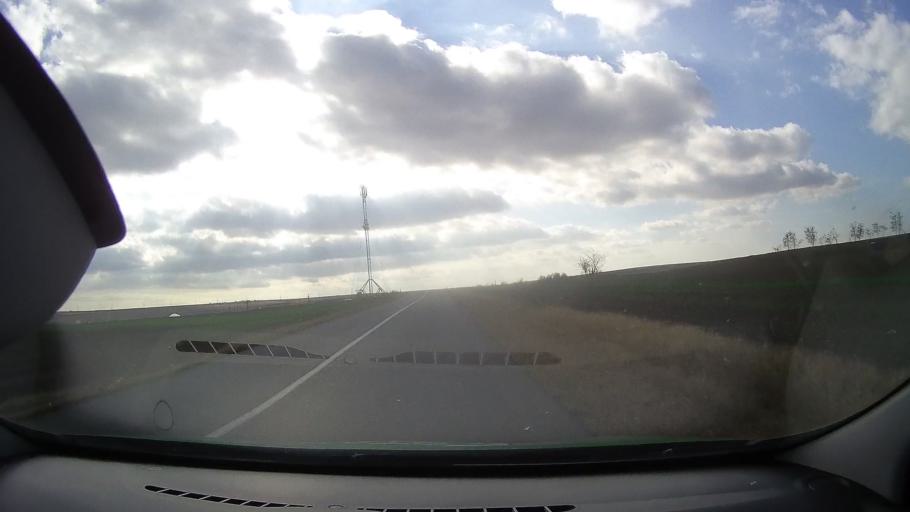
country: RO
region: Constanta
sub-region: Comuna Sacele
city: Sacele
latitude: 44.4931
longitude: 28.6551
